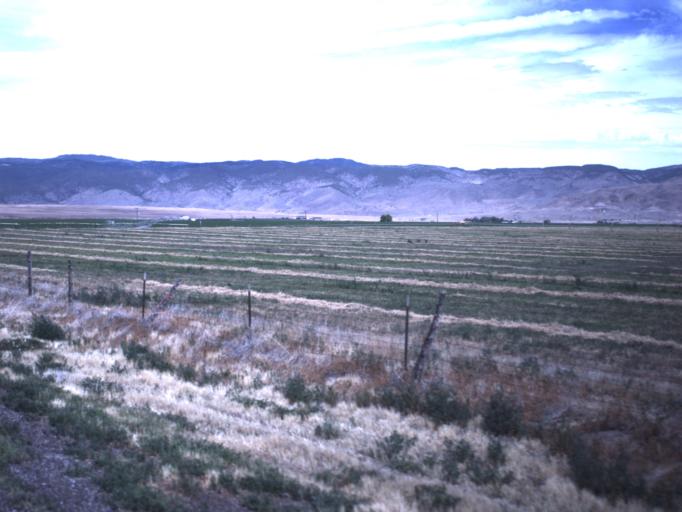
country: US
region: Utah
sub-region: Sevier County
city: Monroe
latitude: 38.6290
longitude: -112.1443
